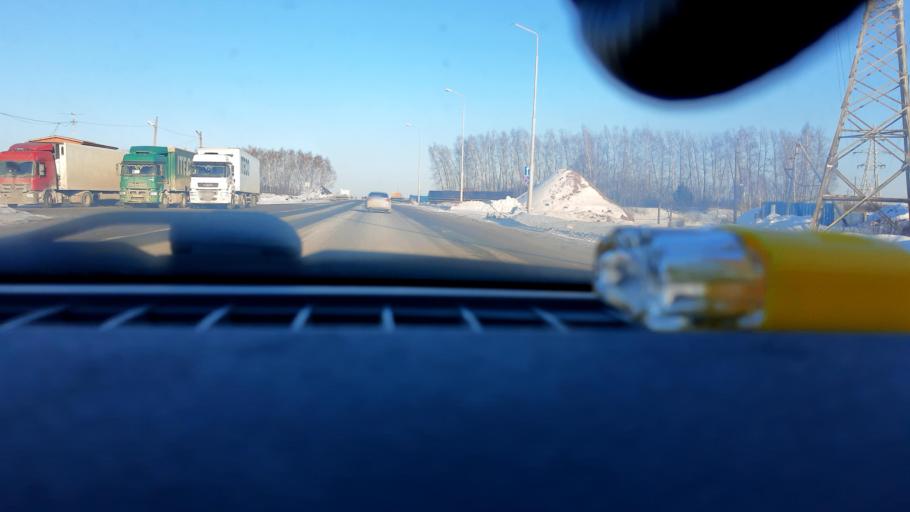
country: RU
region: Bashkortostan
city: Iglino
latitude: 54.7435
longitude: 56.3078
